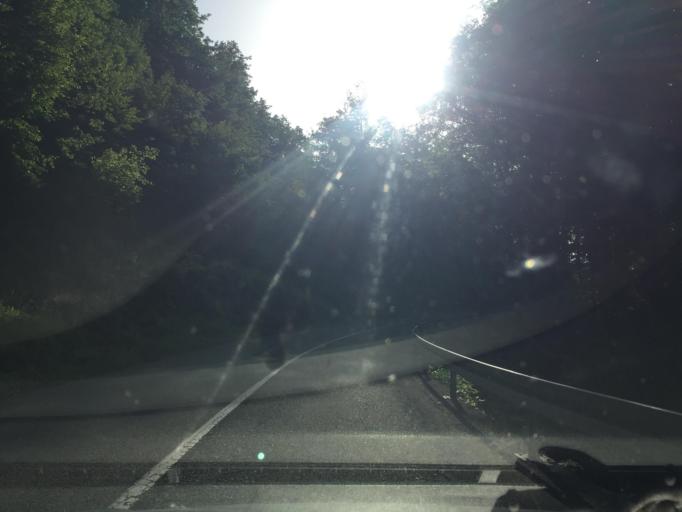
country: HR
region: Primorsko-Goranska
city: Matulji
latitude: 45.4250
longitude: 14.2207
